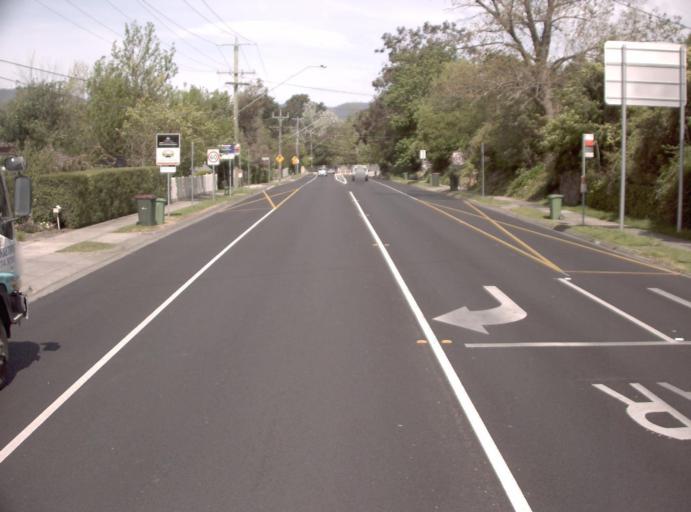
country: AU
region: Victoria
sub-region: Maroondah
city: Croydon Hills
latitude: -37.7871
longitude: 145.2757
